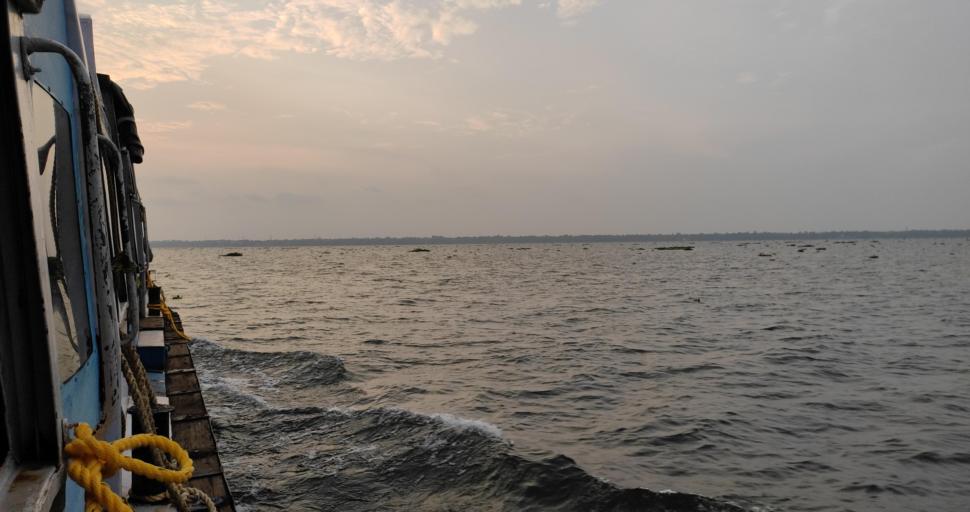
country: IN
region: Kerala
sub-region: Alappuzha
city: Shertallai
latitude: 9.6034
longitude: 76.3860
